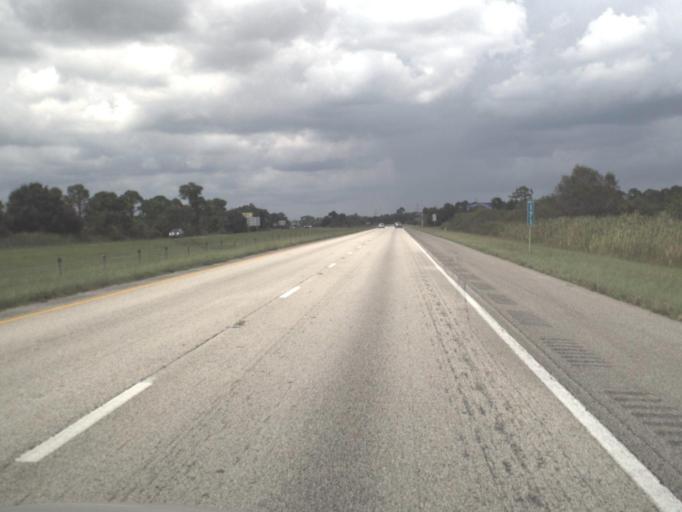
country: US
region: Florida
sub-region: Charlotte County
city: Harbour Heights
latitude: 27.0282
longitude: -82.0531
